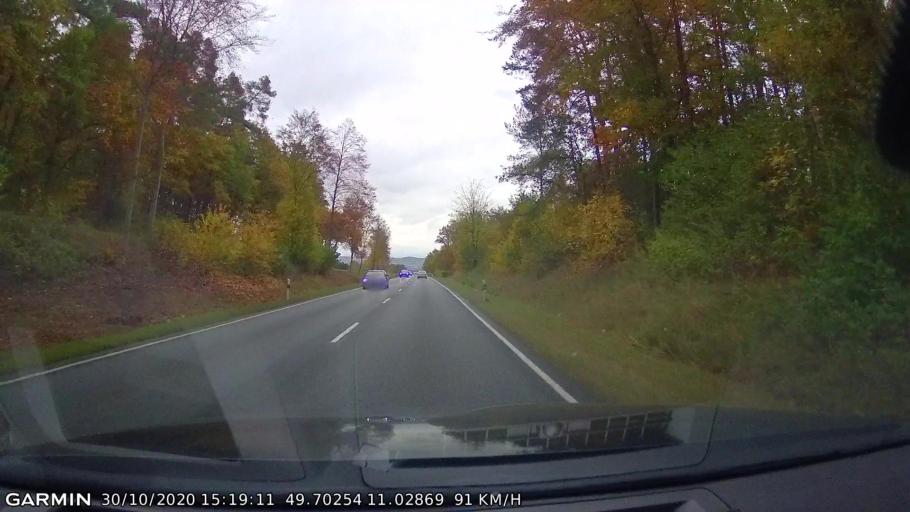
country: DE
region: Bavaria
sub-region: Upper Franconia
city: Hausen
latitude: 49.7025
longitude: 11.0291
